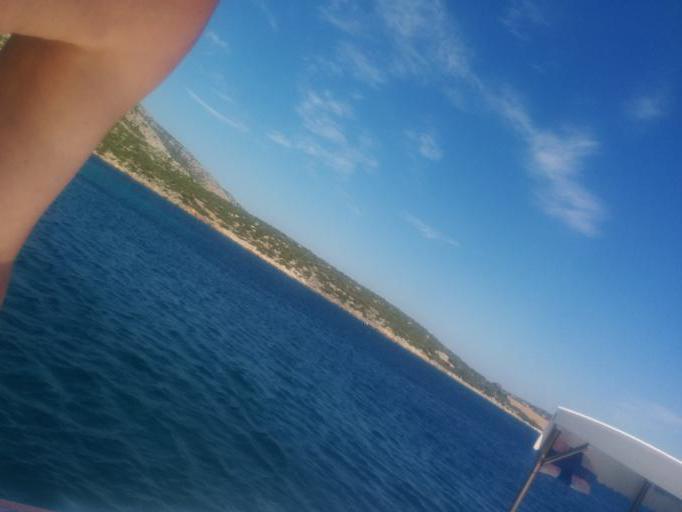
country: GR
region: South Aegean
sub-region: Nomos Dodekanisou
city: Astypalaia
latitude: 36.5826
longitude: 26.4218
